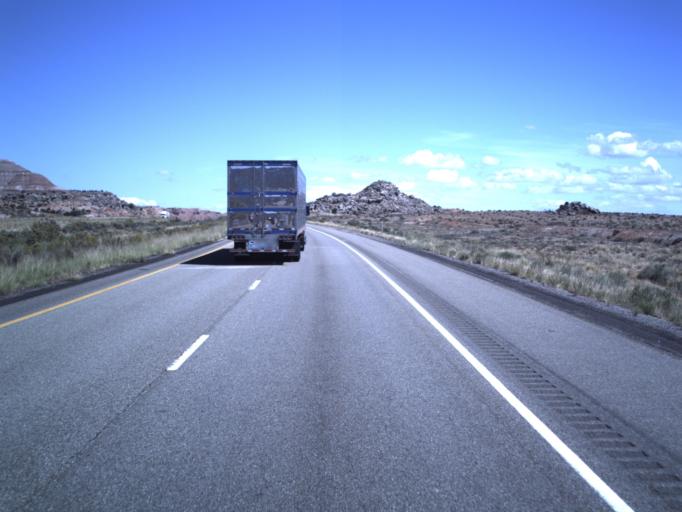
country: US
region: Utah
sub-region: Emery County
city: Ferron
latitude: 38.8200
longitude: -111.1533
